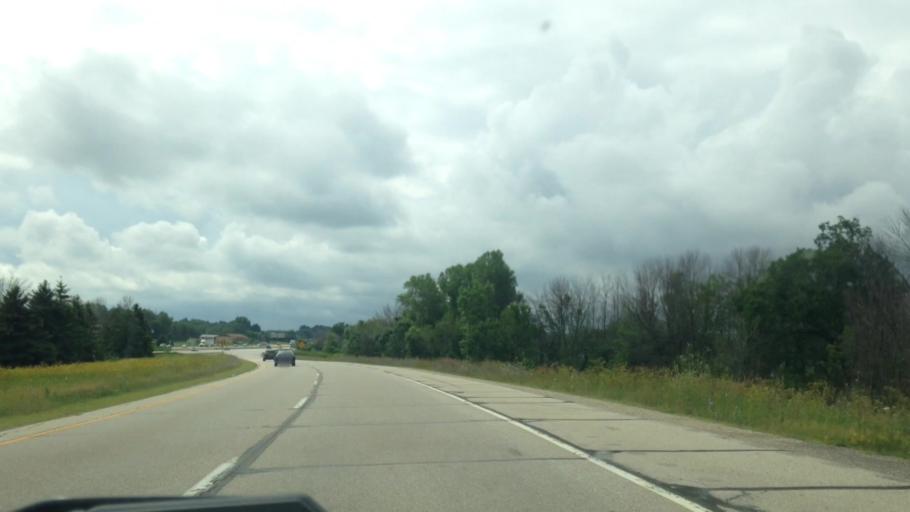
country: US
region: Wisconsin
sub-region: Washington County
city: Richfield
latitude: 43.2717
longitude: -88.1859
